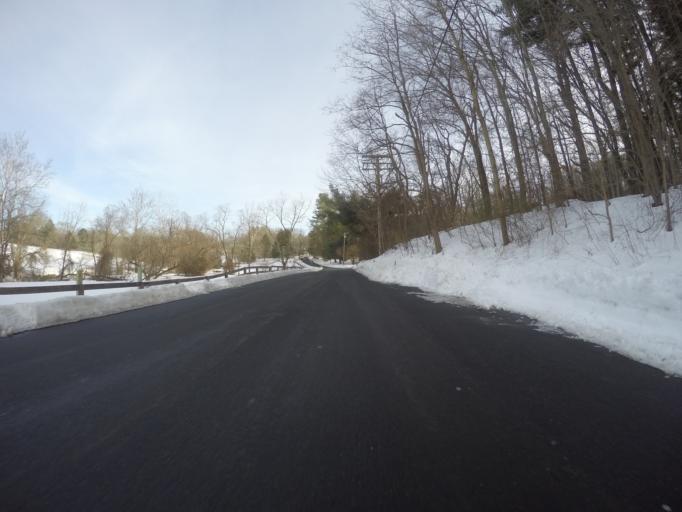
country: US
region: Maryland
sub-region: Baltimore County
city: Hunt Valley
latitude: 39.5608
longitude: -76.6078
